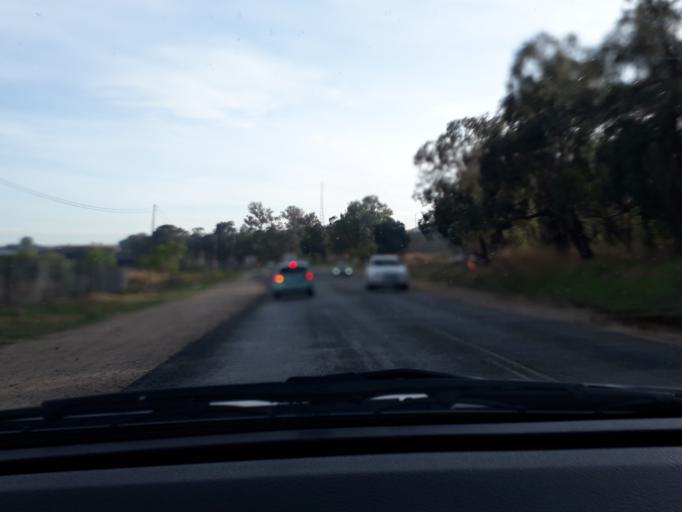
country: ZA
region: Gauteng
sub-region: City of Tshwane Metropolitan Municipality
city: Centurion
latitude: -25.9178
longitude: 28.1558
